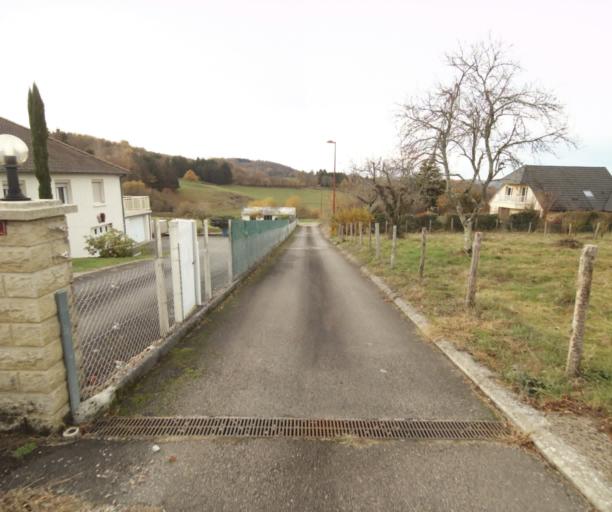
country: FR
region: Limousin
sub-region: Departement de la Correze
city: Sainte-Fortunade
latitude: 45.2103
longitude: 1.7705
